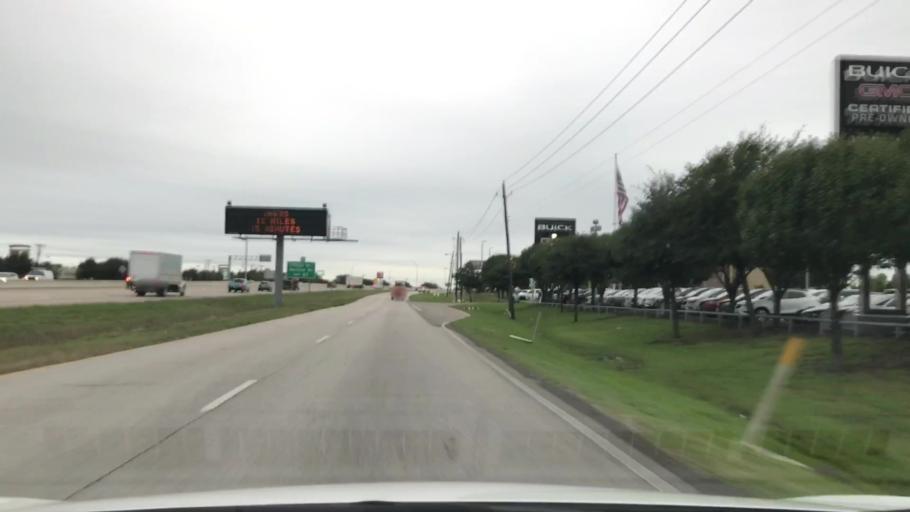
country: US
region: Texas
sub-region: Rockwall County
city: Rockwall
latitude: 32.9045
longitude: -96.4546
